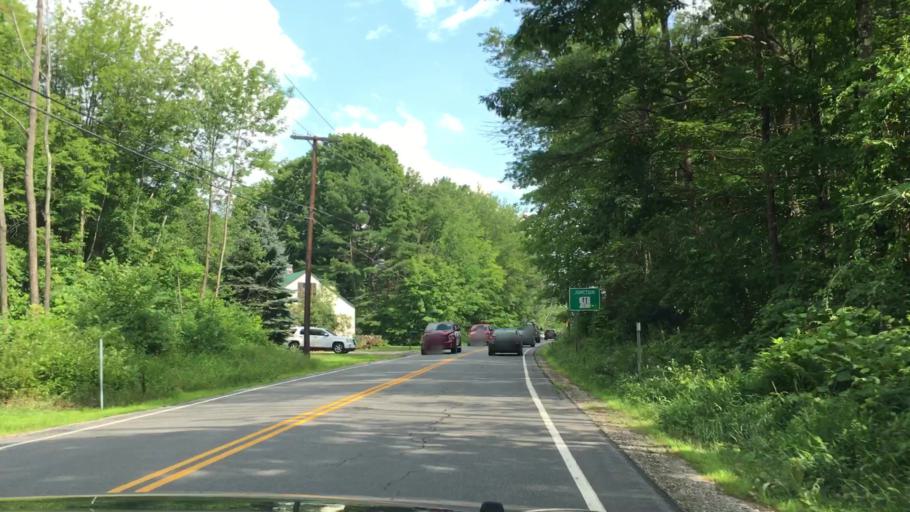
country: US
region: New Hampshire
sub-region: Belknap County
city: Gilford
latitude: 43.5907
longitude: -71.4232
